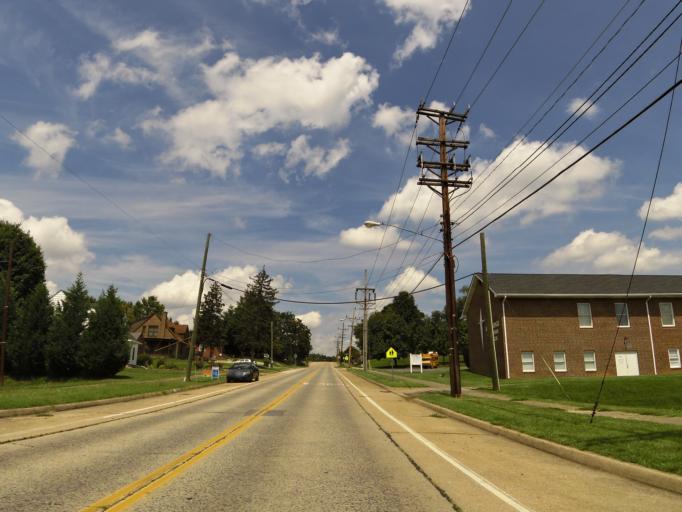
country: US
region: Tennessee
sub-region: Sullivan County
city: Kingsport
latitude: 36.5573
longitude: -82.5658
